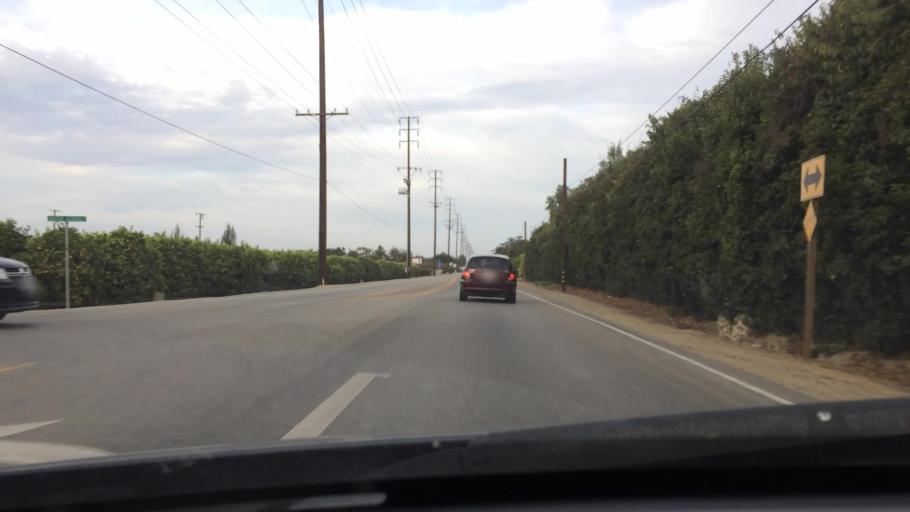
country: US
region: California
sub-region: Ventura County
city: Camarillo
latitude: 34.2637
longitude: -119.0607
